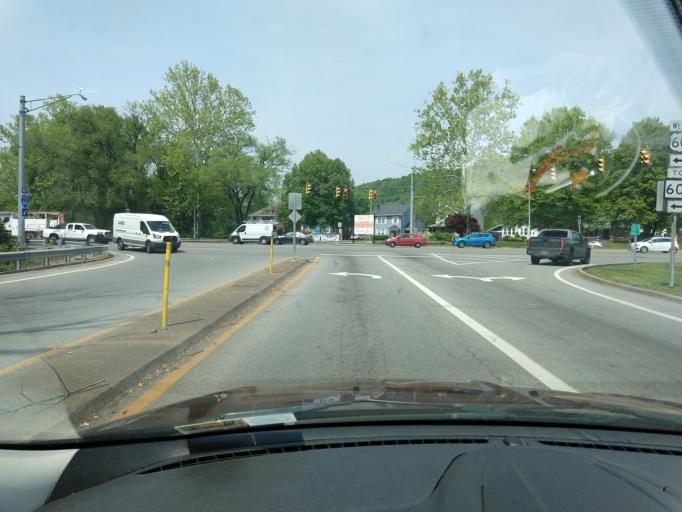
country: US
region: West Virginia
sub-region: Kanawha County
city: South Charleston
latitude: 38.3616
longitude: -81.7144
